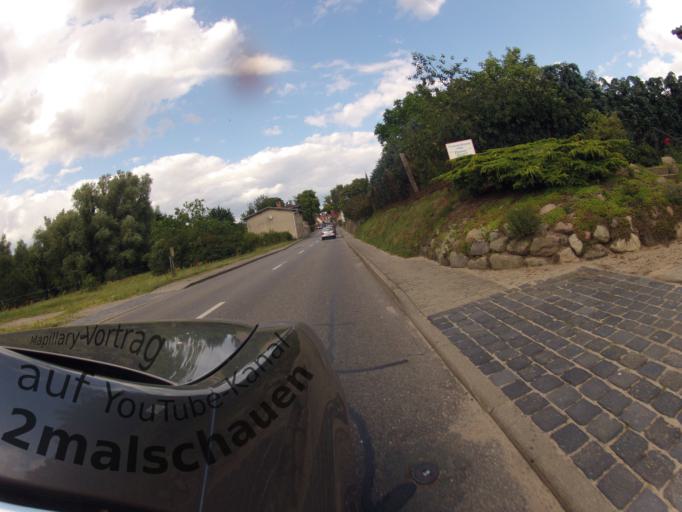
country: DE
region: Mecklenburg-Vorpommern
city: Seebad Heringsdorf
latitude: 53.8884
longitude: 14.1375
